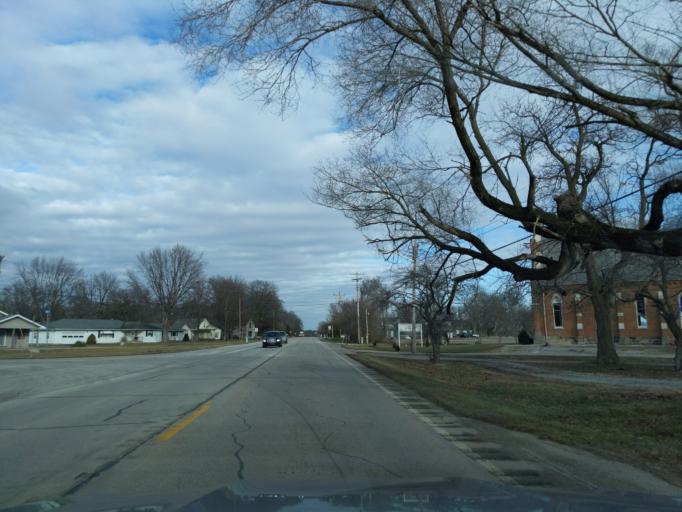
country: US
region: Indiana
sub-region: Tippecanoe County
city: Shadeland
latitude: 40.3735
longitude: -86.9490
